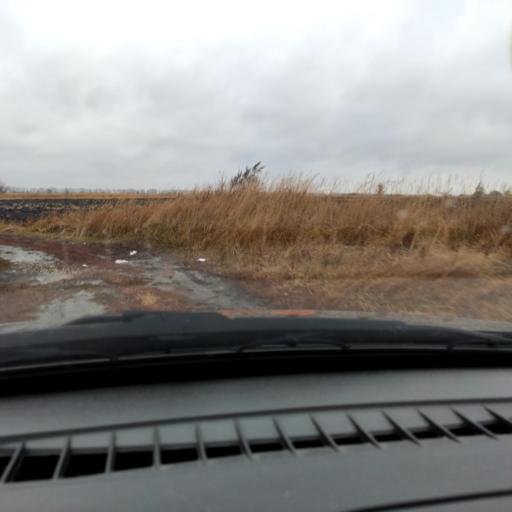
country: RU
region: Samara
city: Khryashchevka
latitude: 53.7154
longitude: 49.2206
